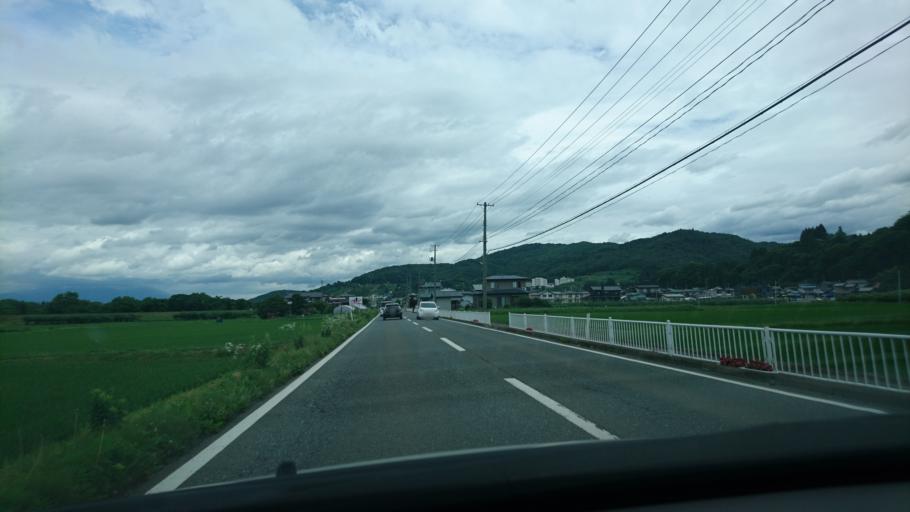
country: JP
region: Iwate
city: Morioka-shi
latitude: 39.6469
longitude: 141.1842
